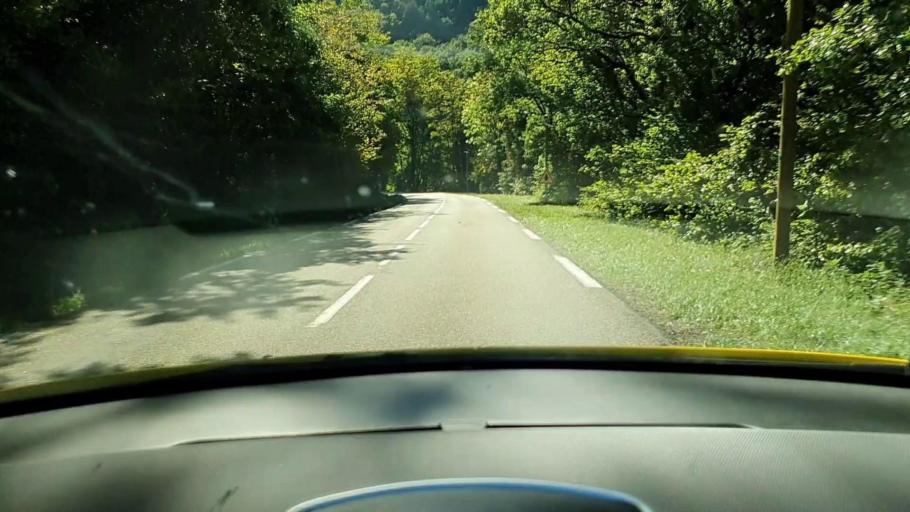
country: FR
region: Languedoc-Roussillon
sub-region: Departement du Gard
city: Le Vigan
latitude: 43.9688
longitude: 3.4177
